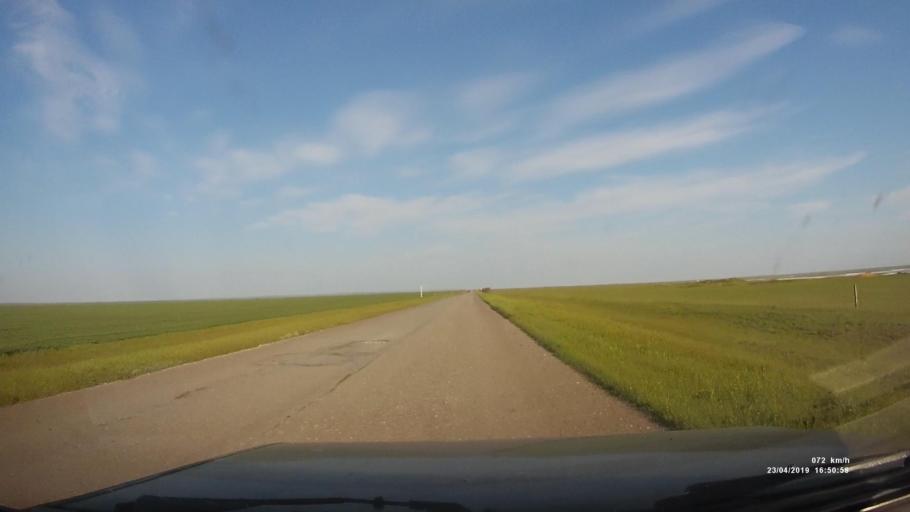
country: RU
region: Kalmykiya
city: Priyutnoye
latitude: 46.3249
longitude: 43.2995
